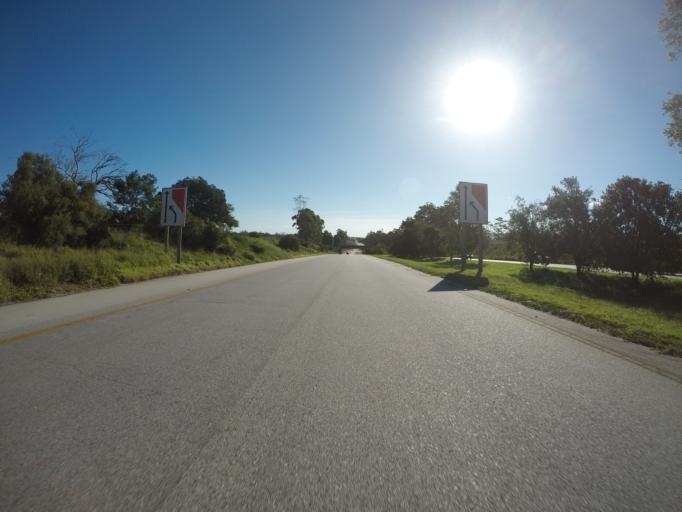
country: ZA
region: Eastern Cape
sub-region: Nelson Mandela Bay Metropolitan Municipality
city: Uitenhage
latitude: -33.8973
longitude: 25.1599
